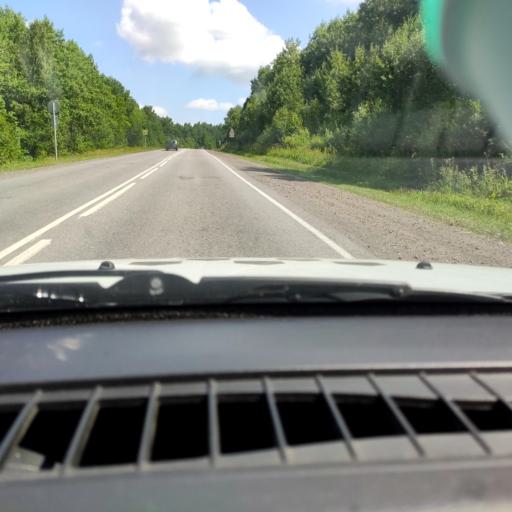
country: RU
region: Bashkortostan
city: Verkhniye Kigi
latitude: 55.3857
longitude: 58.6698
